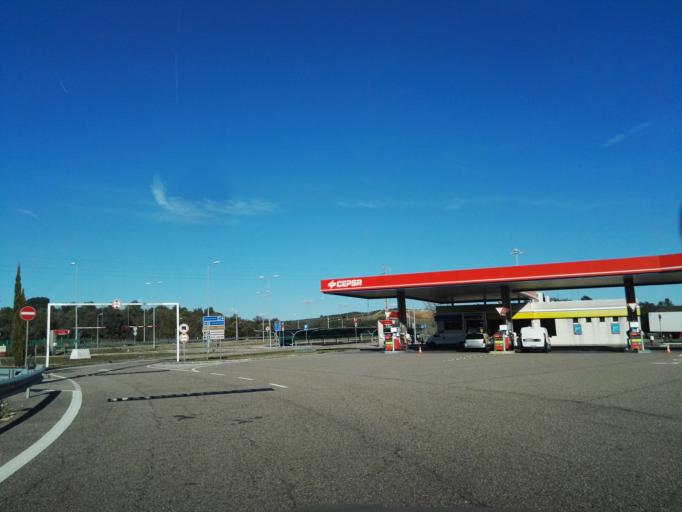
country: PT
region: Santarem
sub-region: Abrantes
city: Alferrarede
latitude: 39.4847
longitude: -8.1560
